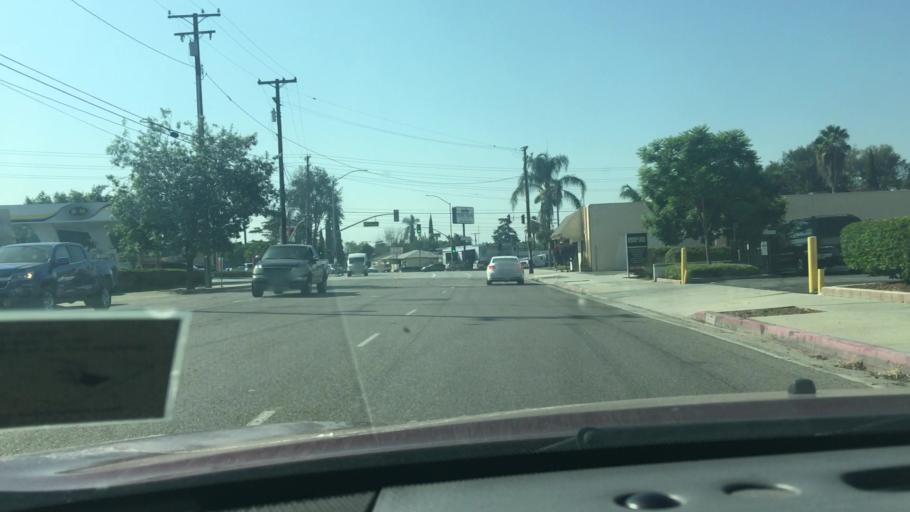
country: US
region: California
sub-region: Los Angeles County
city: South Whittier
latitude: 33.9646
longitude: -118.0465
